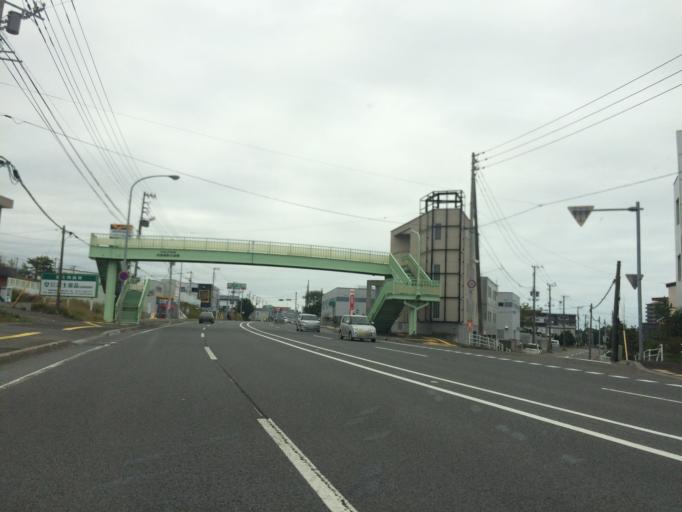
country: JP
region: Hokkaido
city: Sapporo
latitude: 43.1220
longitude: 141.2285
